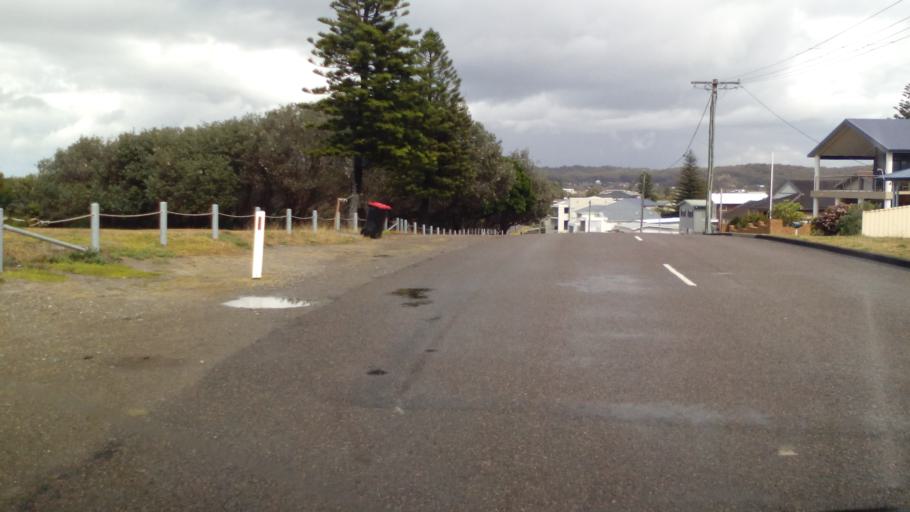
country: AU
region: New South Wales
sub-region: Lake Macquarie Shire
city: Belmont South
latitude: -33.0946
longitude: 151.6595
